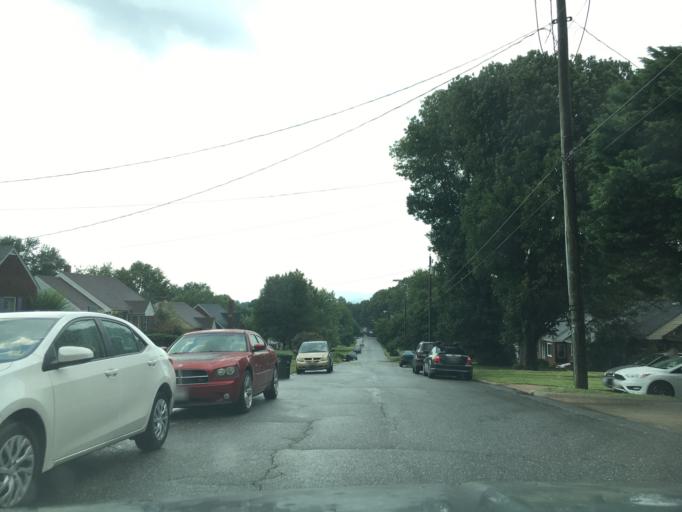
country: US
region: Virginia
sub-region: City of Lynchburg
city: West Lynchburg
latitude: 37.3774
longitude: -79.1860
